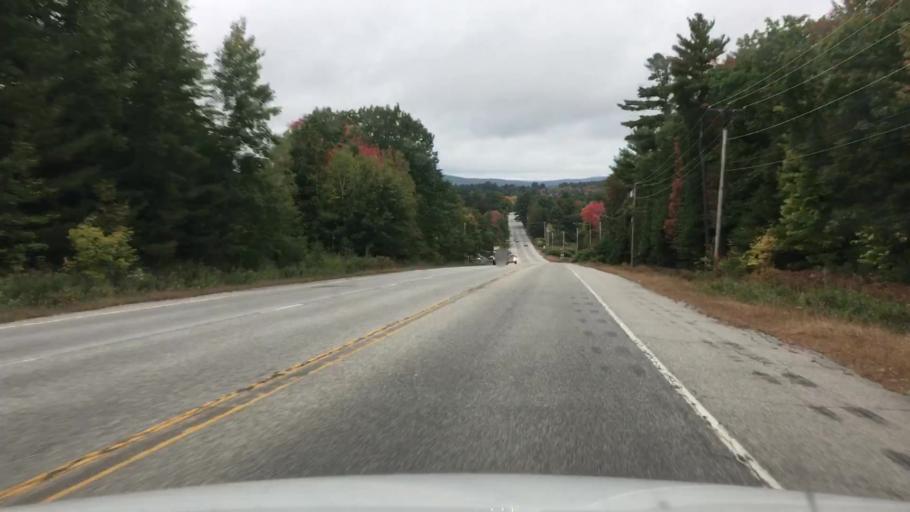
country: US
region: Maine
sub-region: Oxford County
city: Oxford
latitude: 44.1245
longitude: -70.4505
